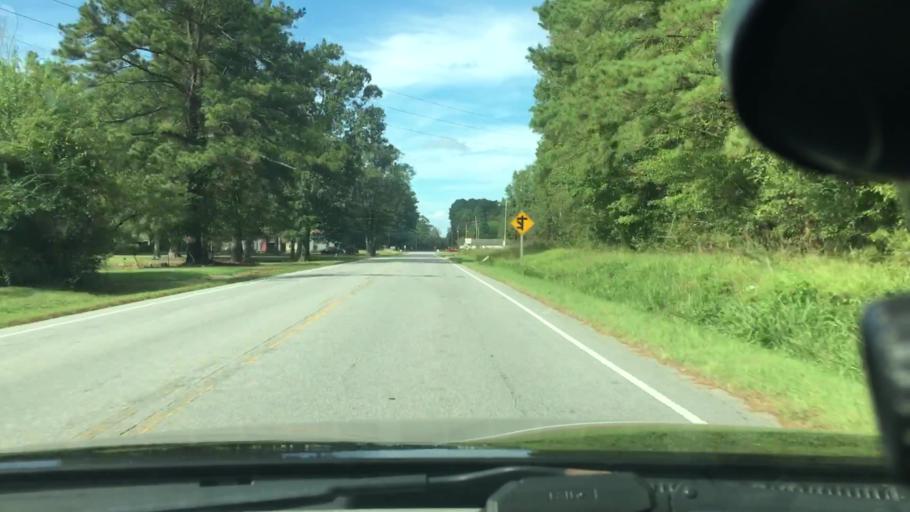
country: US
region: North Carolina
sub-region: Pitt County
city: Windsor
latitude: 35.4461
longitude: -77.2635
